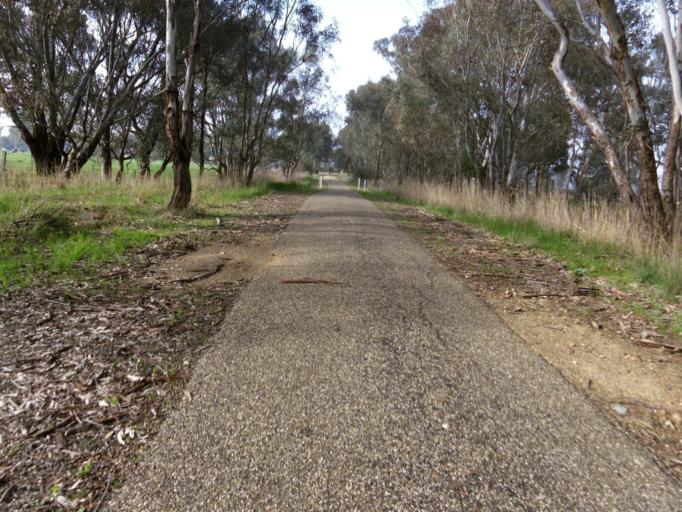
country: AU
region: Victoria
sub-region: Wangaratta
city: Wangaratta
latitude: -36.4514
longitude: 146.5530
